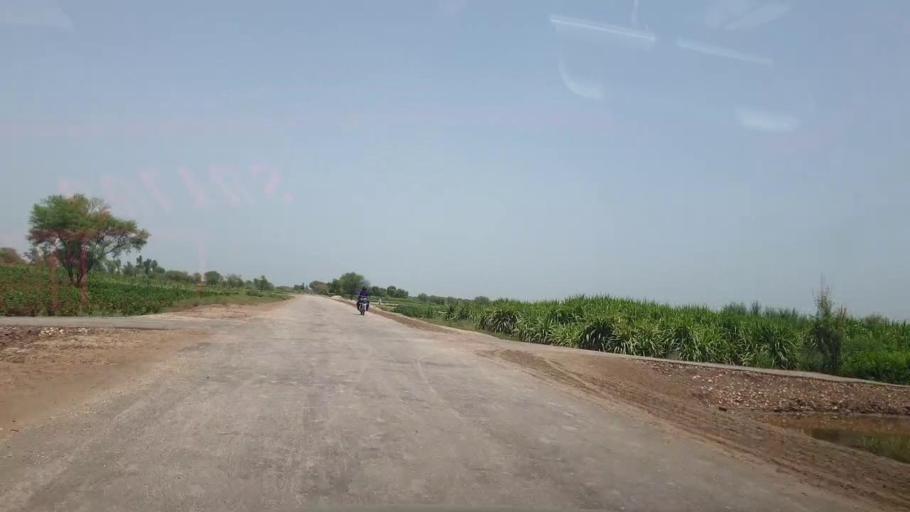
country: PK
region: Sindh
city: Daulatpur
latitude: 26.3894
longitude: 68.0925
